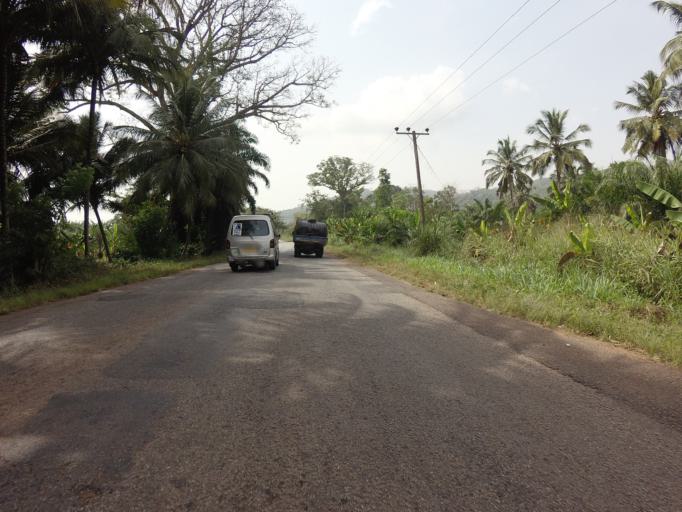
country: GH
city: Akropong
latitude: 6.2902
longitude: 0.1322
